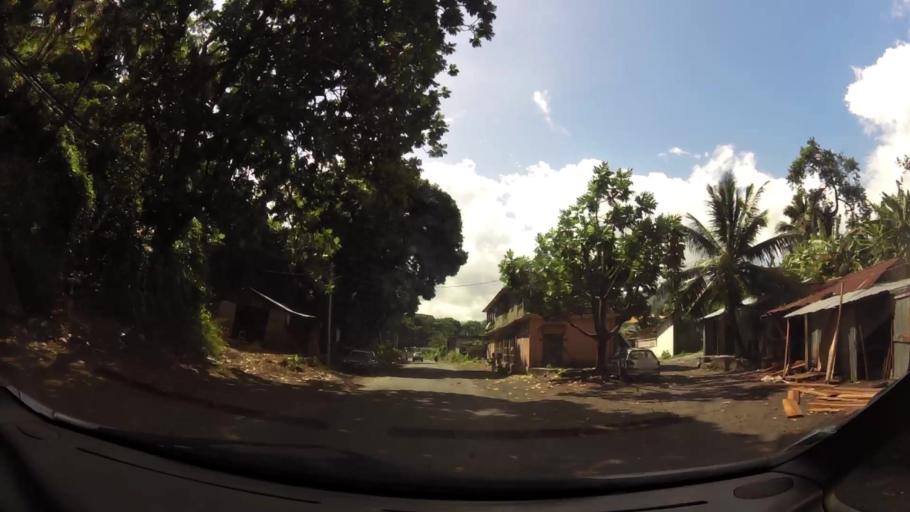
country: KM
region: Grande Comore
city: Mavingouni
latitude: -11.7240
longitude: 43.2500
